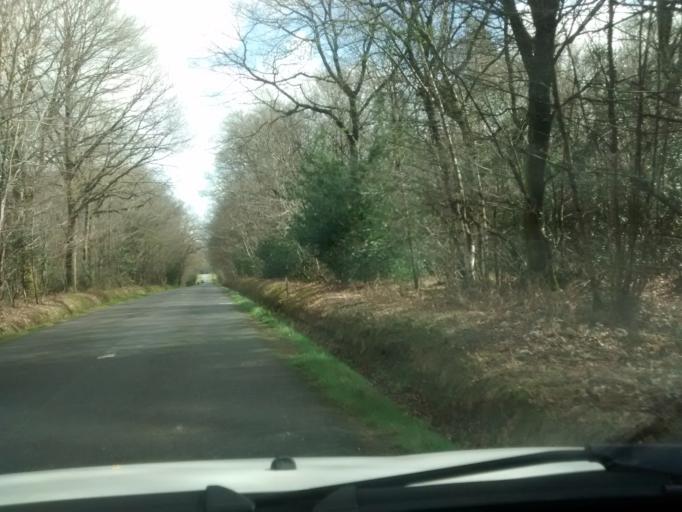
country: FR
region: Brittany
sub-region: Departement d'Ille-et-Vilaine
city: Servon-sur-Vilaine
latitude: 48.1639
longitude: -1.4824
